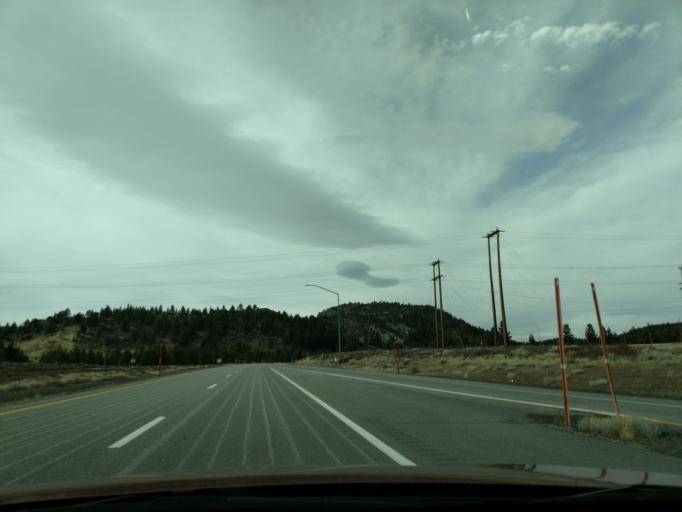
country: US
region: California
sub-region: Mono County
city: Mammoth Lakes
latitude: 37.6429
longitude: -118.9191
